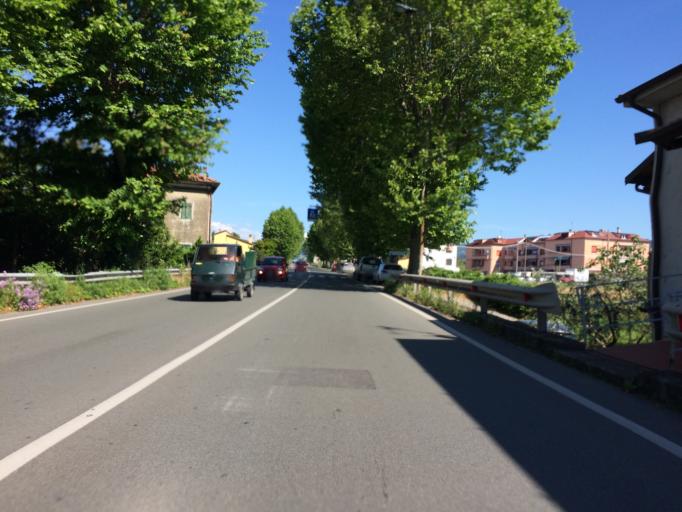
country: IT
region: Liguria
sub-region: Provincia di La Spezia
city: Colombiera-Molicciara
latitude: 44.0797
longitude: 10.0109
